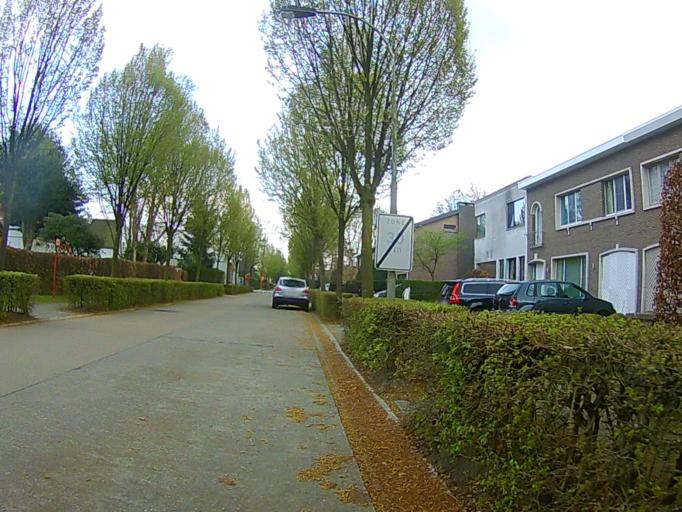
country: BE
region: Flanders
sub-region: Provincie Antwerpen
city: Kapellen
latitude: 51.2983
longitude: 4.4488
